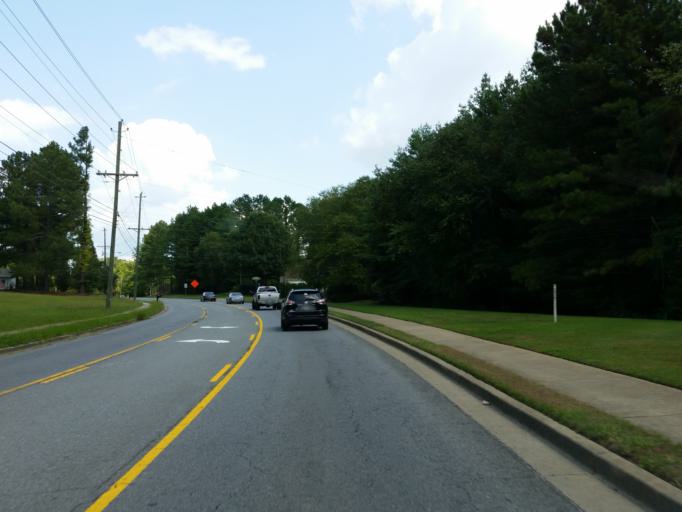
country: US
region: Georgia
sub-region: Fulton County
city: Sandy Springs
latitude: 33.9498
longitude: -84.4503
